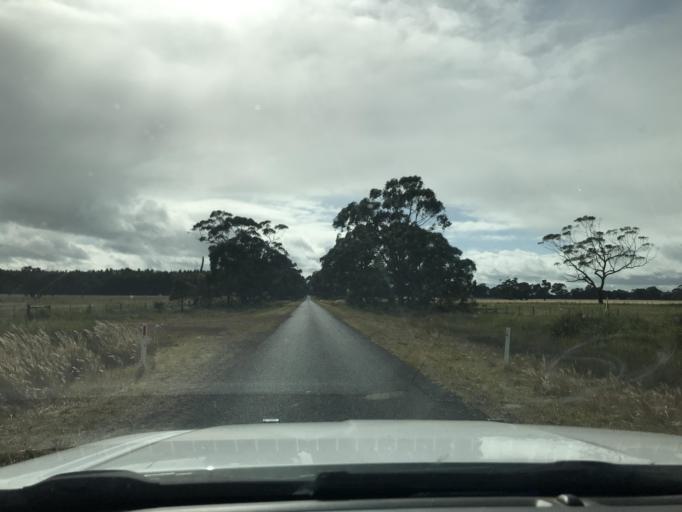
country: AU
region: South Australia
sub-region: Wattle Range
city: Penola
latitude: -37.1860
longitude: 141.2142
